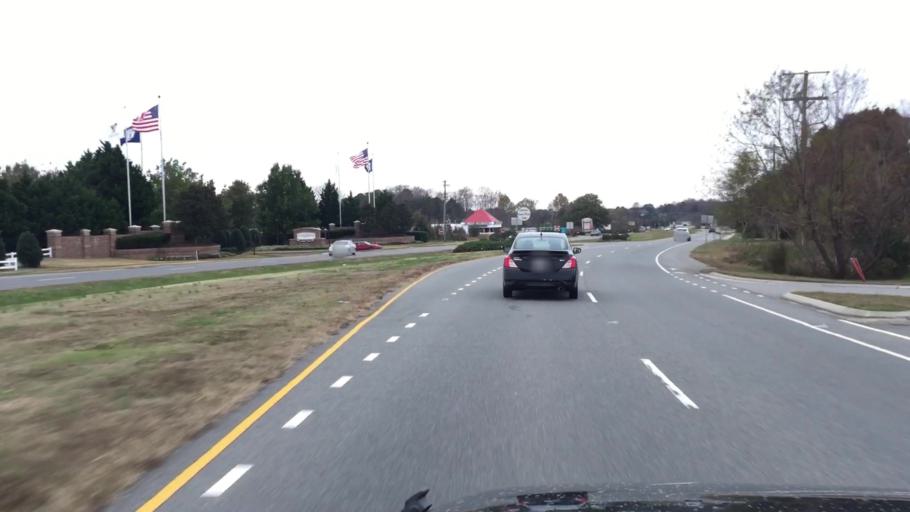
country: US
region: Virginia
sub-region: James City County
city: Williamsburg
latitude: 37.3521
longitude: -76.7634
